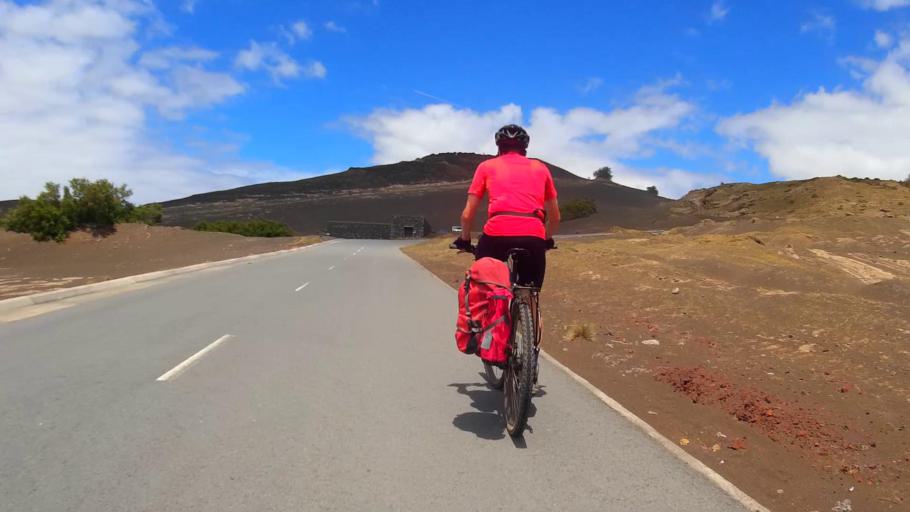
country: PT
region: Azores
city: Ribeira Grande
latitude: 38.5956
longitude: -28.8233
